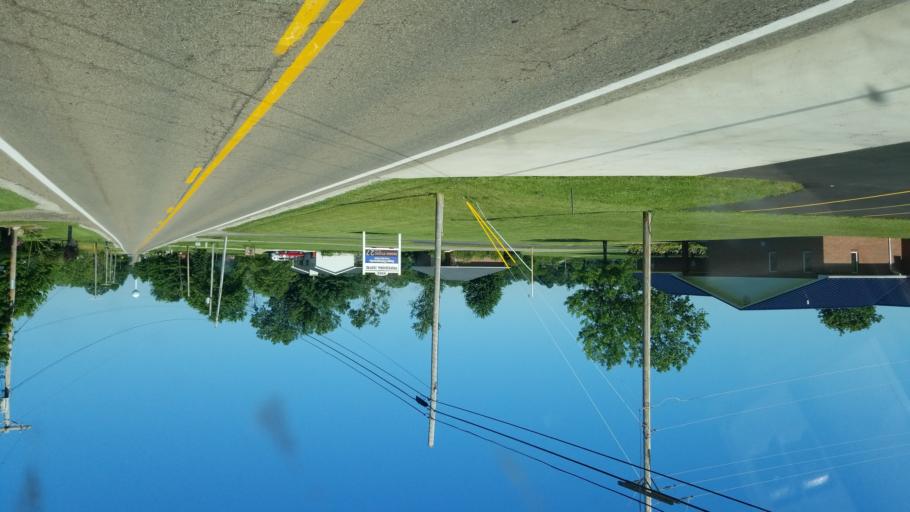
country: US
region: Ohio
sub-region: Morrow County
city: Cardington
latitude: 40.4017
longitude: -82.7993
